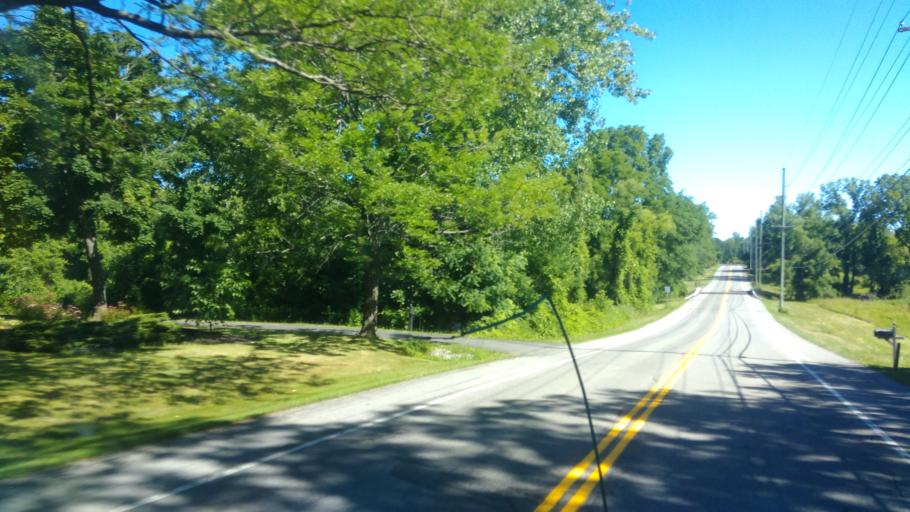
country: US
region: New York
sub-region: Monroe County
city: Webster
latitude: 43.2636
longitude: -77.4009
